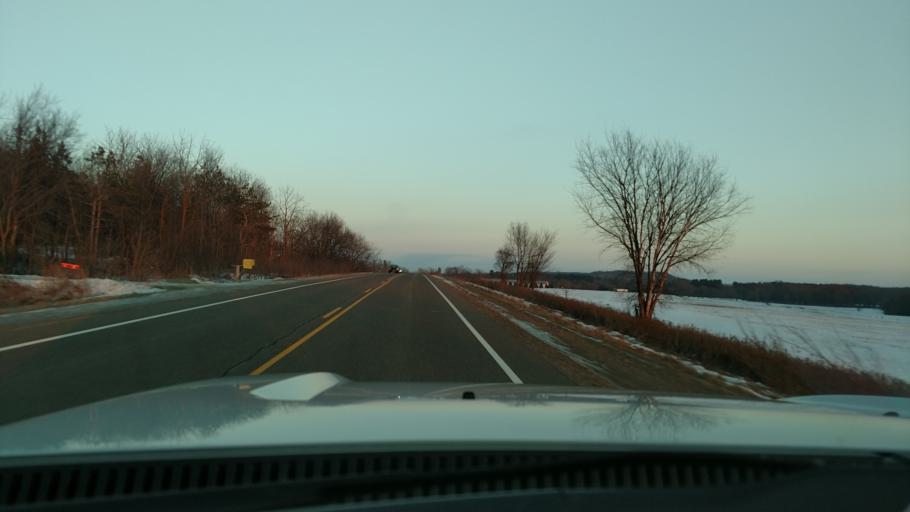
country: US
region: Wisconsin
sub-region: Pierce County
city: River Falls
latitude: 44.9037
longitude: -92.5719
